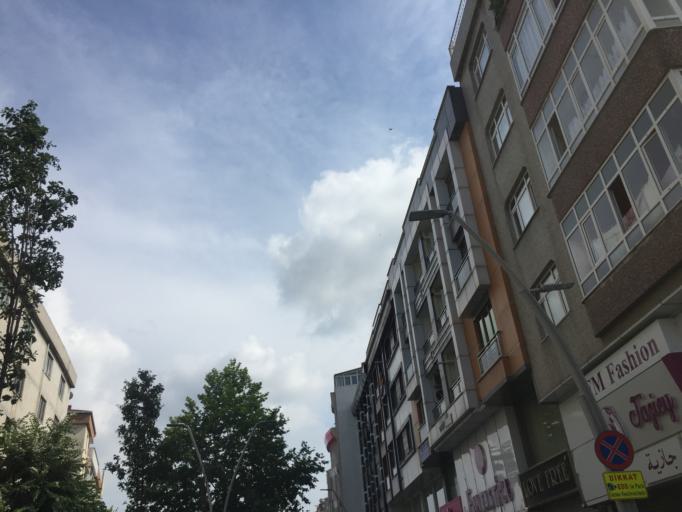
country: TR
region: Istanbul
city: Zeytinburnu
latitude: 41.0004
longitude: 28.9042
